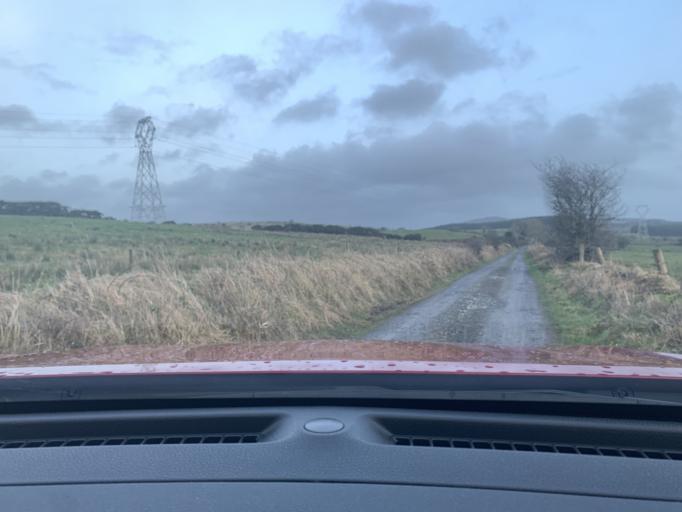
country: IE
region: Connaught
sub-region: Sligo
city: Ballymote
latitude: 53.9930
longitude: -8.4372
